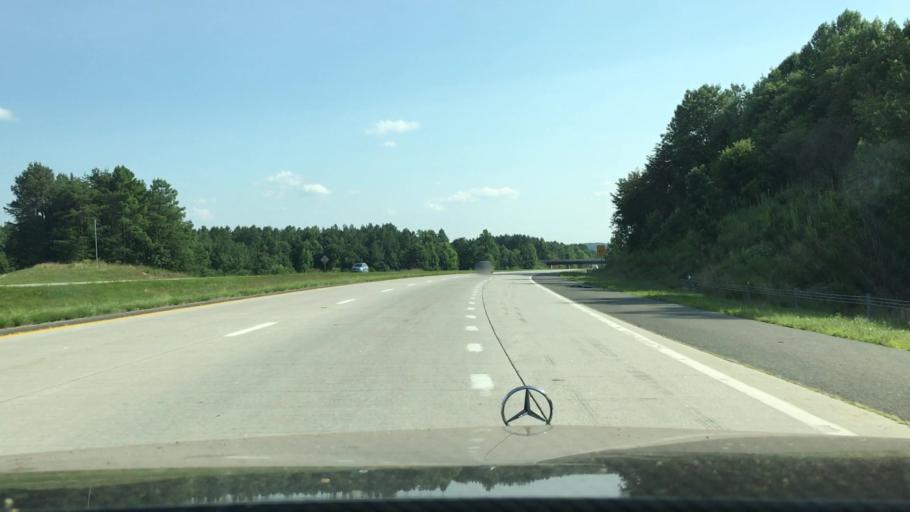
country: US
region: Virginia
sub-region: Amherst County
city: Madison Heights
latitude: 37.4120
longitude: -79.0823
